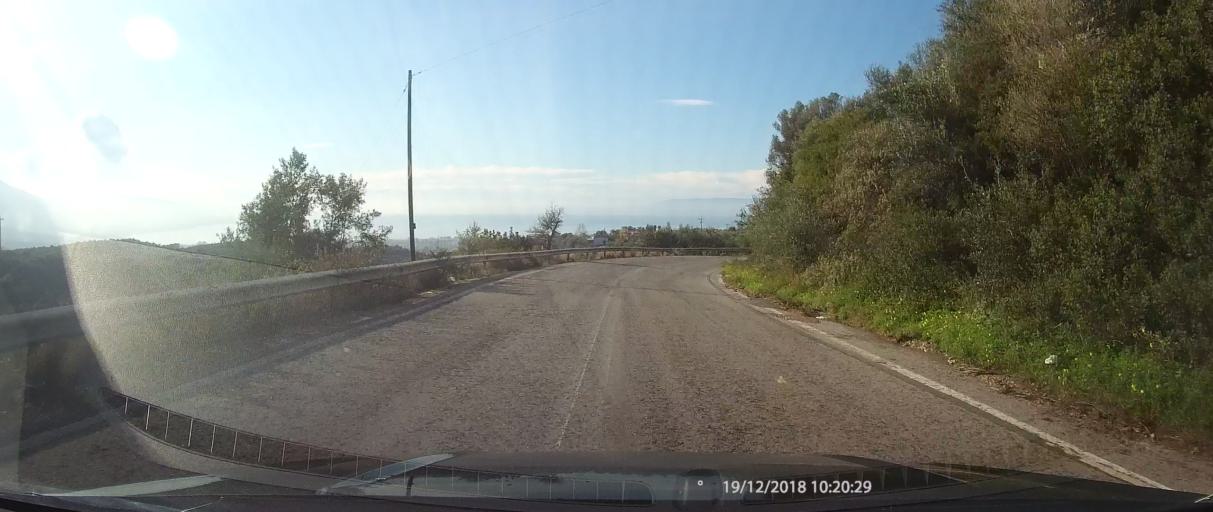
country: GR
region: Peloponnese
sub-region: Nomos Messinias
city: Kalamata
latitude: 37.0532
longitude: 22.1414
